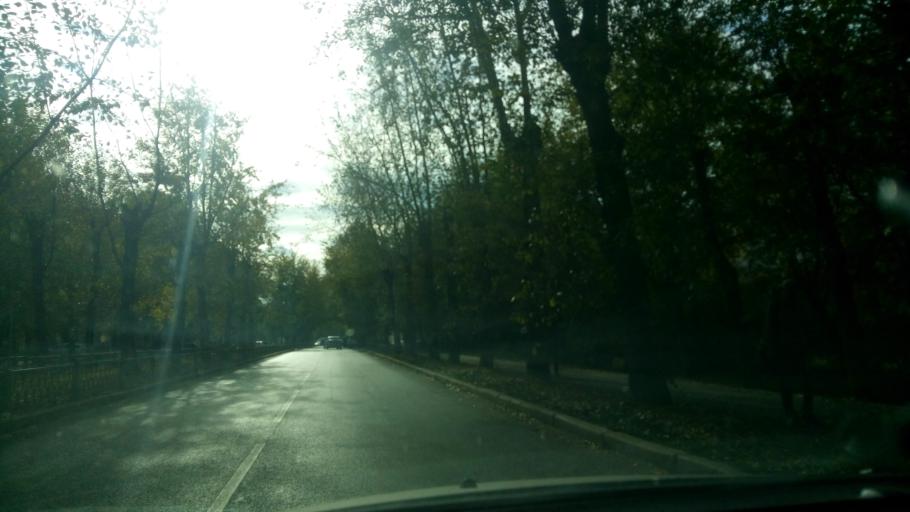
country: RU
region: Sverdlovsk
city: Yekaterinburg
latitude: 56.8884
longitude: 60.6176
